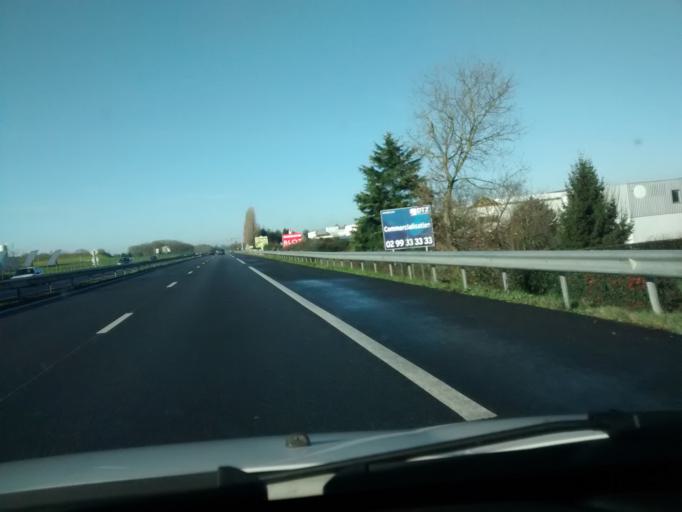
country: FR
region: Brittany
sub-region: Departement d'Ille-et-Vilaine
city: Chateaubourg
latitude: 48.0978
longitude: -1.4110
